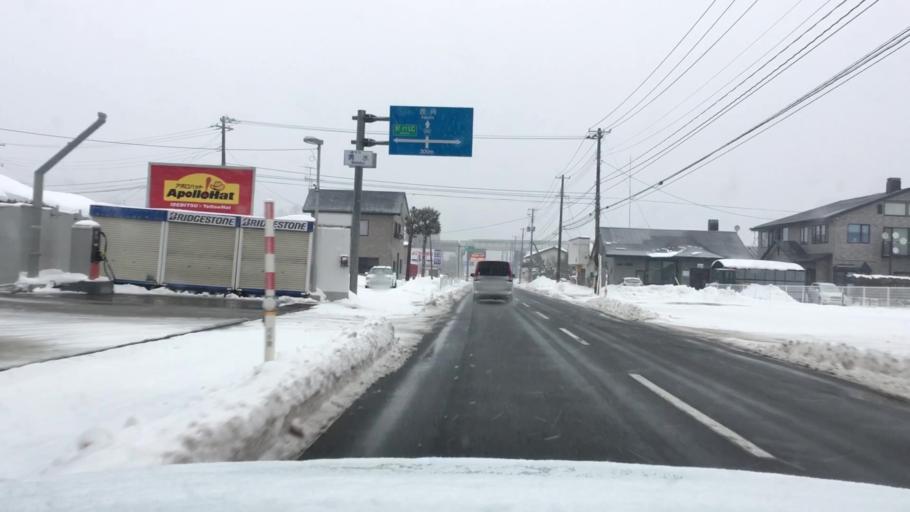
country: JP
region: Iwate
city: Ichinohe
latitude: 40.1068
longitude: 141.0506
